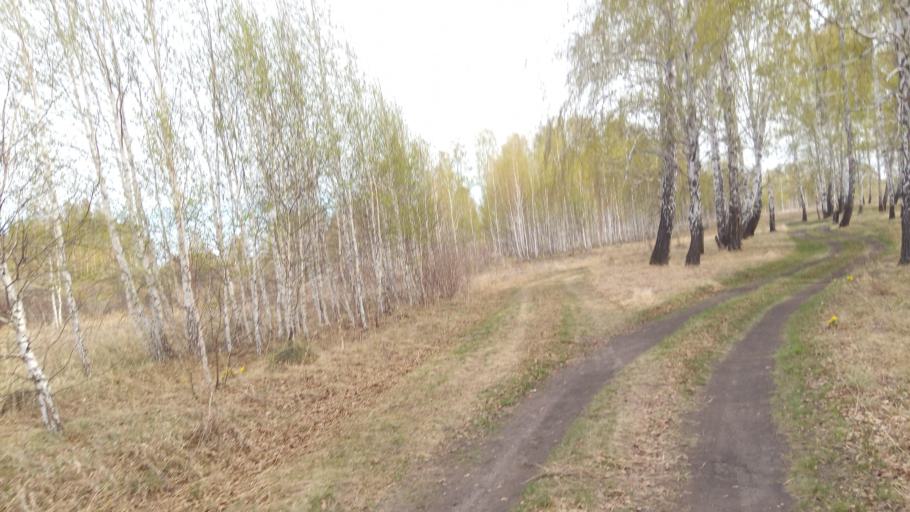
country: RU
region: Chelyabinsk
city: Timiryazevskiy
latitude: 55.0054
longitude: 60.8589
